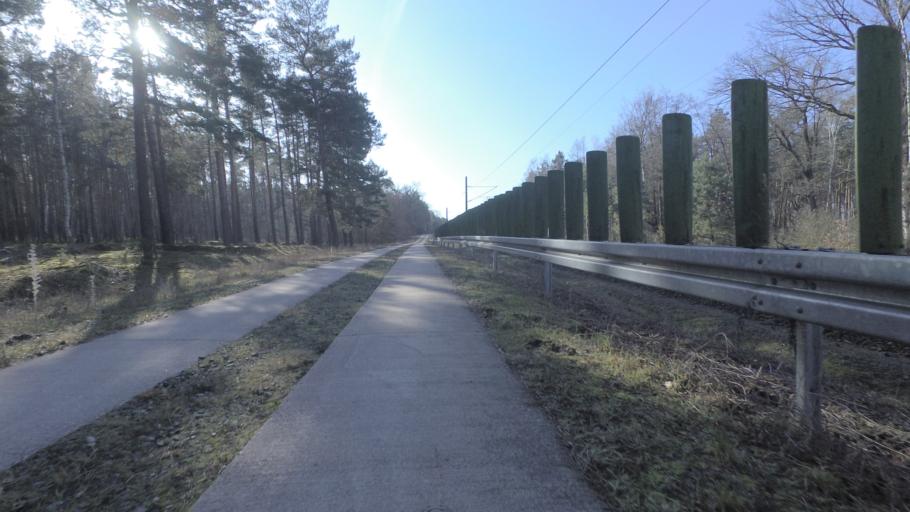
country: DE
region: Brandenburg
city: Luckenwalde
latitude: 52.1373
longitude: 13.2180
